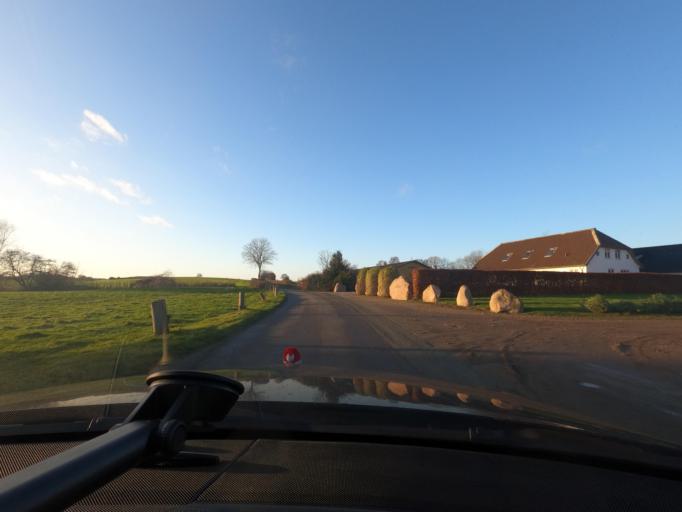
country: DK
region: South Denmark
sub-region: Sonderborg Kommune
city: Broager
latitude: 54.9025
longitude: 9.7003
